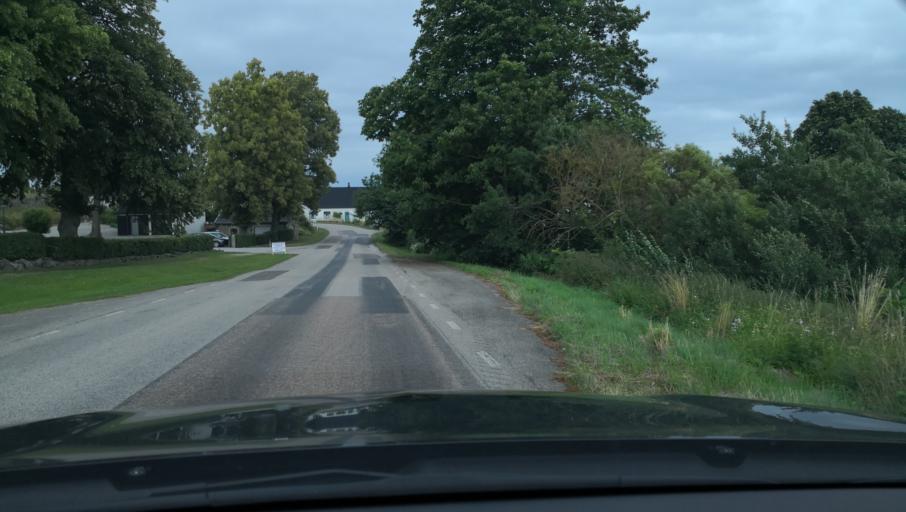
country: SE
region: Skane
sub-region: Simrishamns Kommun
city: Kivik
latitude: 55.6937
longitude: 14.1682
